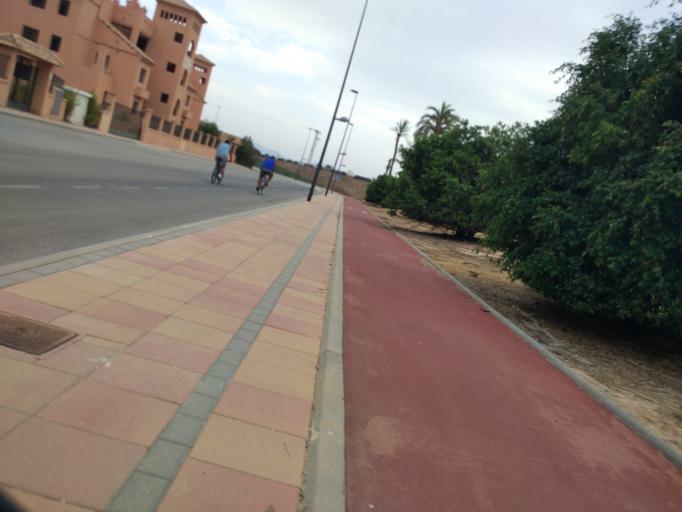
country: ES
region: Murcia
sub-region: Murcia
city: Los Alcazares
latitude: 37.7223
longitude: -0.8698
